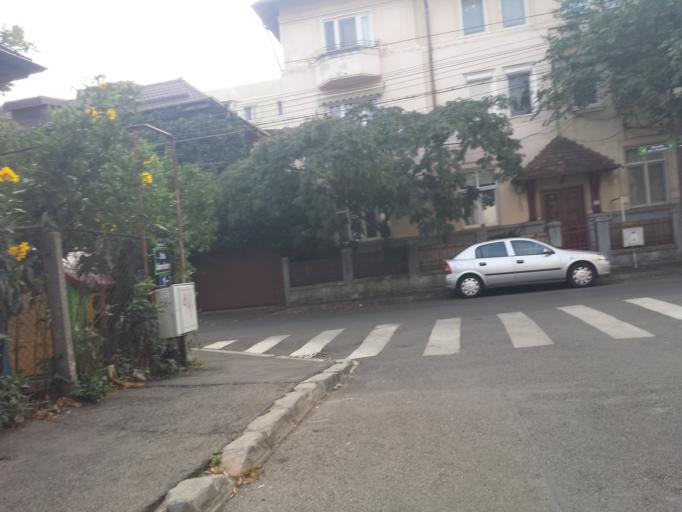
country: RO
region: Ilfov
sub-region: Comuna Chiajna
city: Rosu
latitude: 44.4660
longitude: 26.0588
